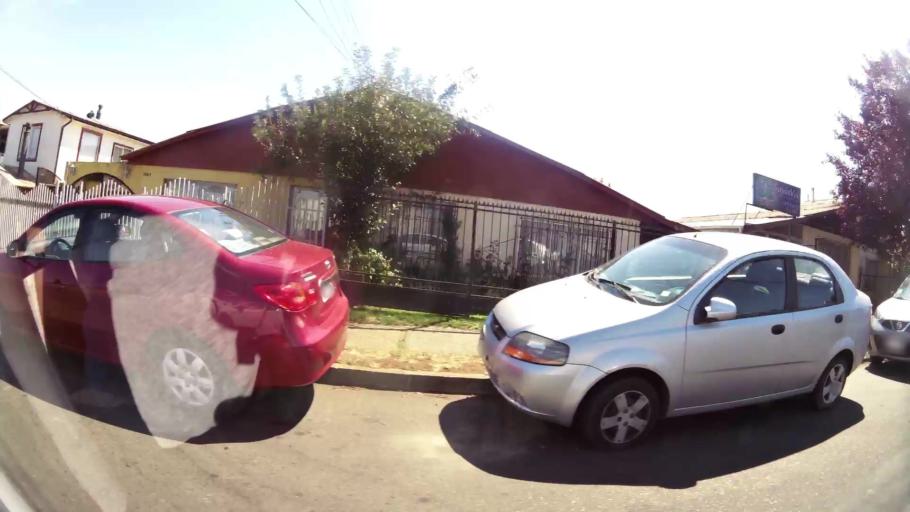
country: CL
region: Biobio
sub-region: Provincia de Concepcion
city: Concepcion
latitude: -36.7882
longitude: -73.0430
